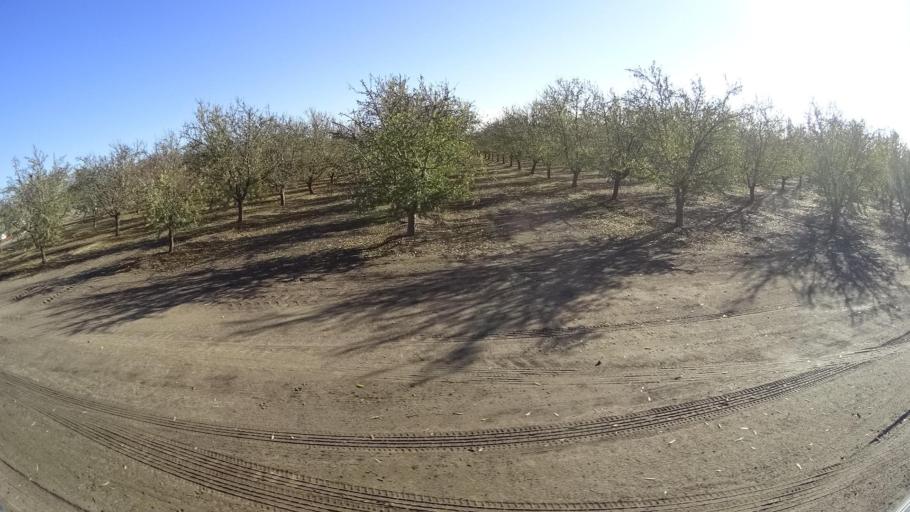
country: US
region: California
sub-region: Kern County
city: Delano
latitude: 35.7246
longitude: -119.3119
